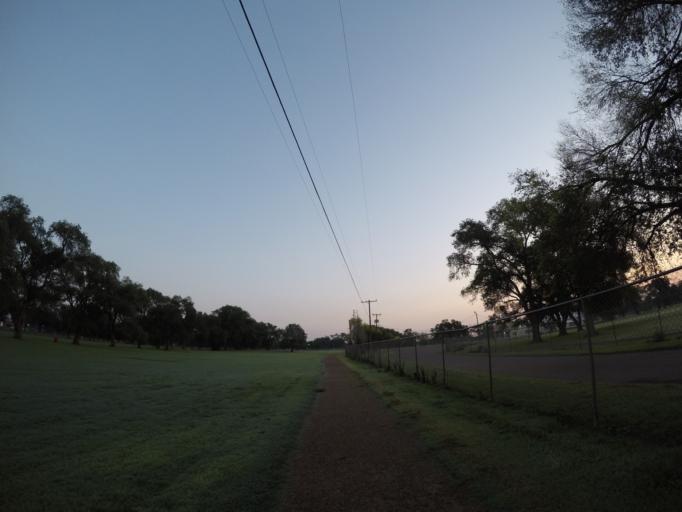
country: US
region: New Mexico
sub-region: Curry County
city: Clovis
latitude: 34.4053
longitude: -103.1856
